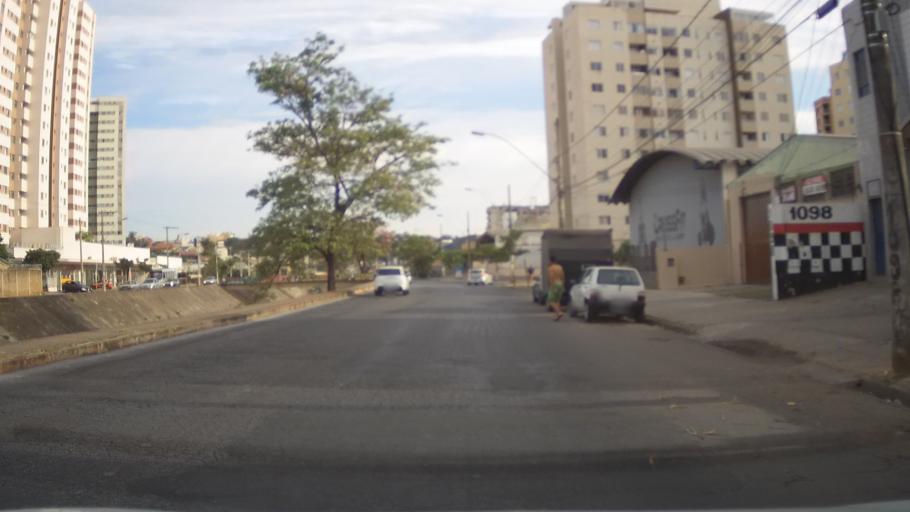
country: BR
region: Minas Gerais
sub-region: Contagem
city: Contagem
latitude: -19.8837
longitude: -44.0059
